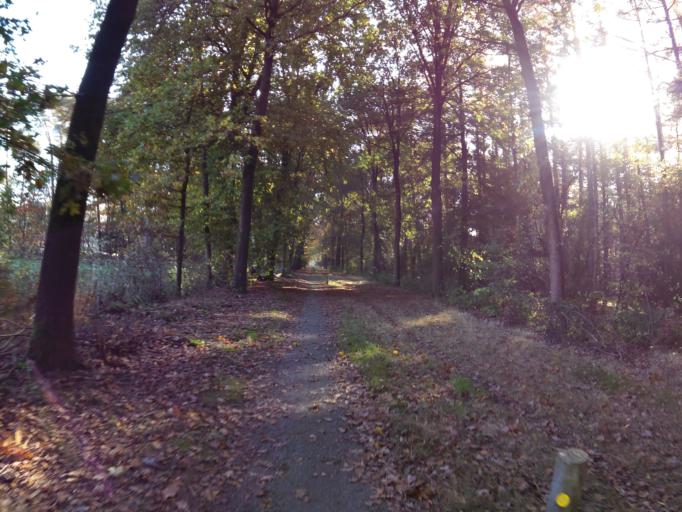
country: NL
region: North Brabant
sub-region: Gemeente Boxtel
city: Boxtel
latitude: 51.6130
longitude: 5.3088
